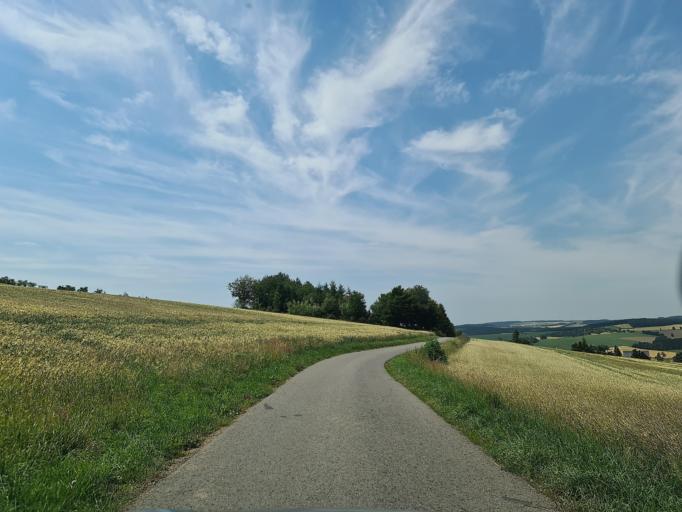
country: DE
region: Saxony
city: Neuhausen
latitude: 50.6603
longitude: 13.4720
